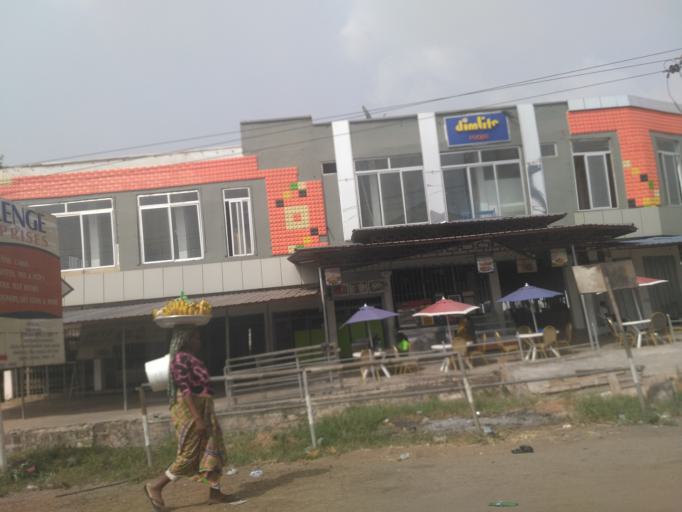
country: GH
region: Ashanti
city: Kumasi
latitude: 6.6876
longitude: -1.5822
